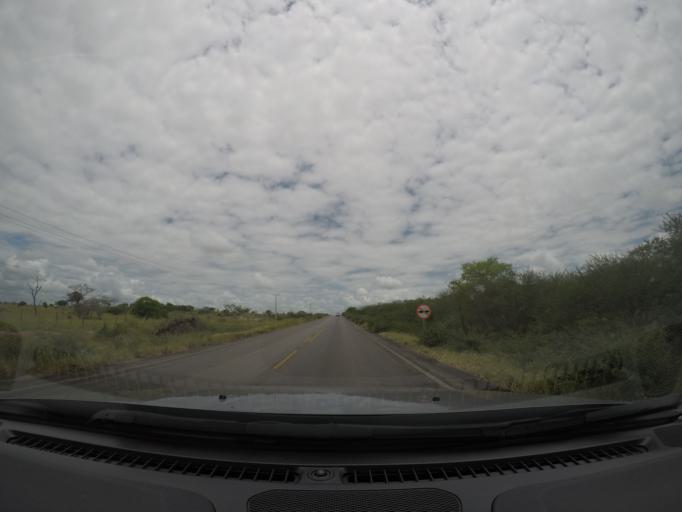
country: BR
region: Bahia
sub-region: Itaberaba
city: Itaberaba
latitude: -12.4844
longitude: -40.2181
